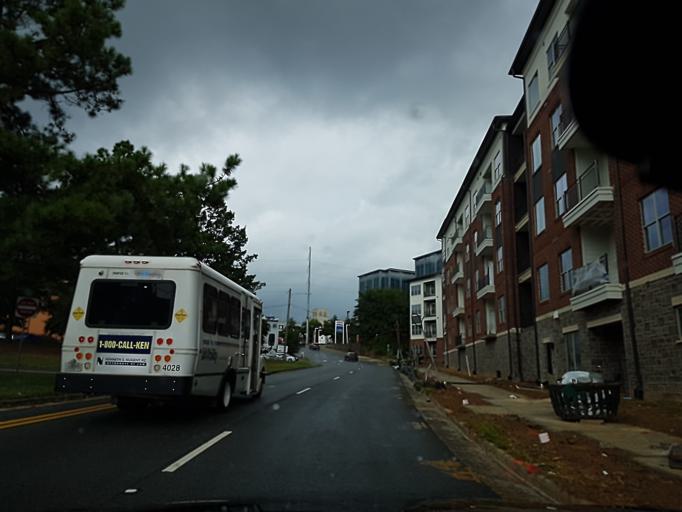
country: US
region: Georgia
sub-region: DeKalb County
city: Druid Hills
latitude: 33.8208
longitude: -84.3657
